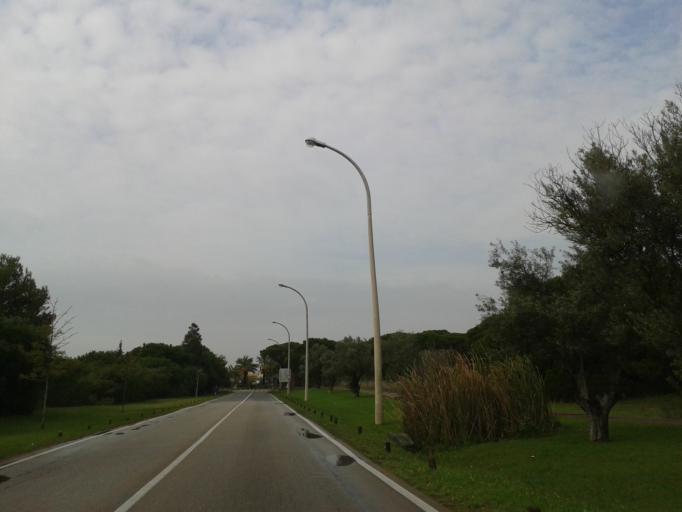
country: PT
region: Faro
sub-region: Loule
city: Vilamoura
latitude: 37.1054
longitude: -8.1329
